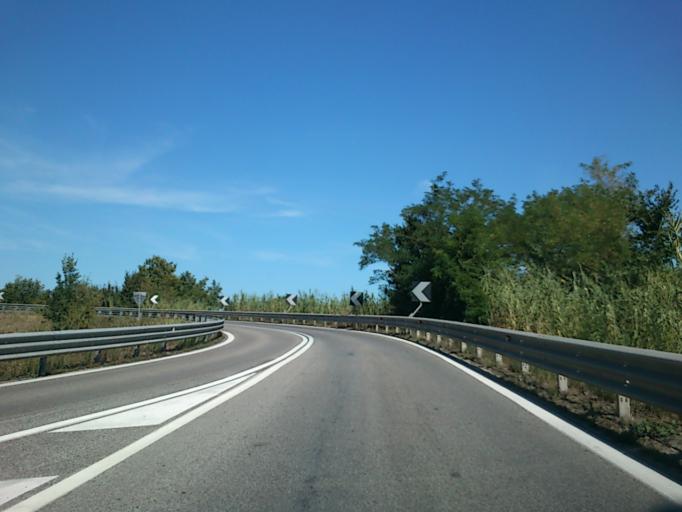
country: IT
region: The Marches
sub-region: Provincia di Pesaro e Urbino
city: Rosciano
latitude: 43.8218
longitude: 13.0158
